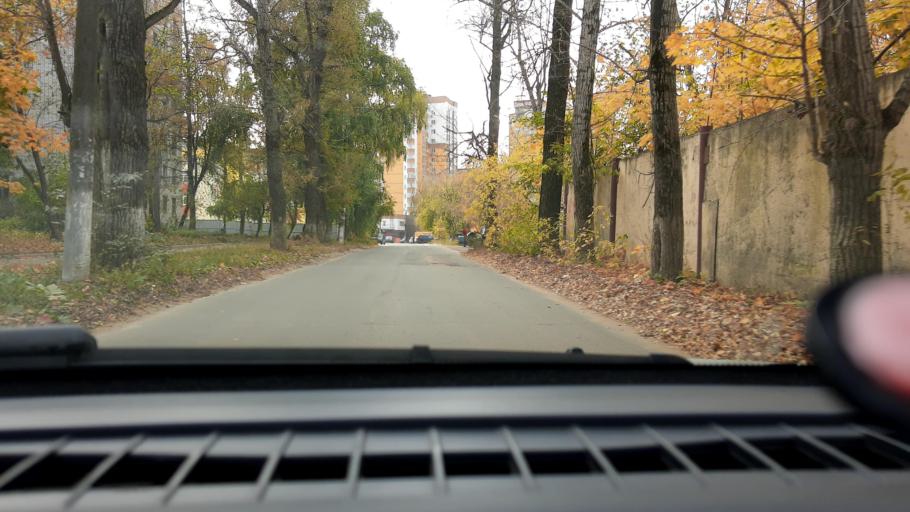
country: RU
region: Nizjnij Novgorod
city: Nizhniy Novgorod
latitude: 56.2390
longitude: 43.9537
